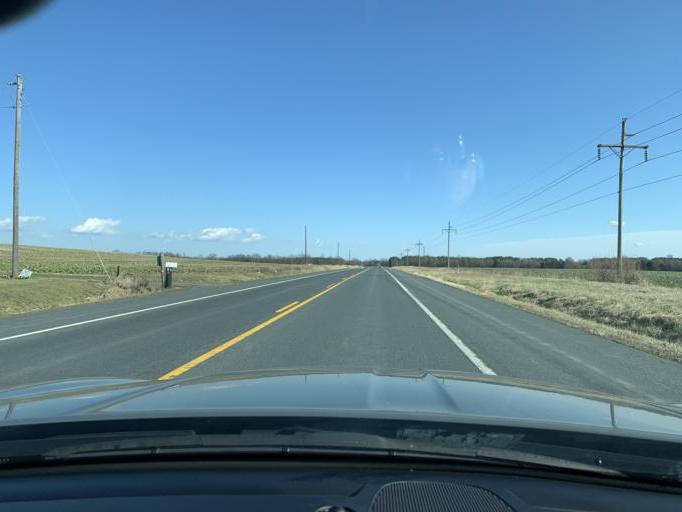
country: US
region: Maryland
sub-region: Queen Anne's County
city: Kingstown
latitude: 39.2562
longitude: -75.9574
